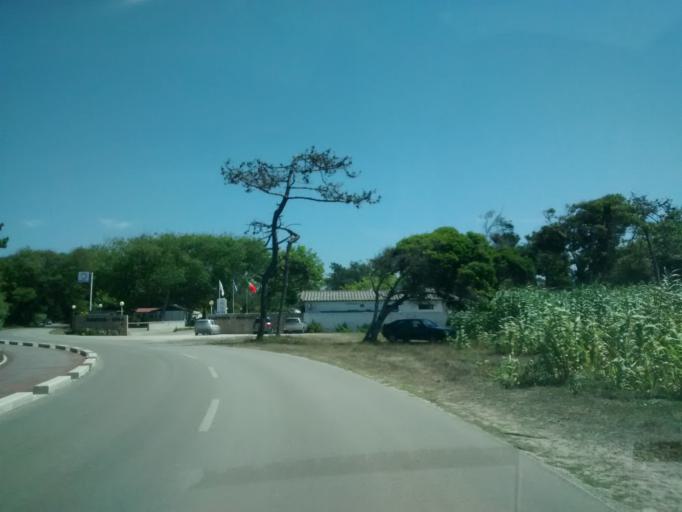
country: PT
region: Coimbra
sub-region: Mira
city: Mira
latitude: 40.4450
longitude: -8.8028
